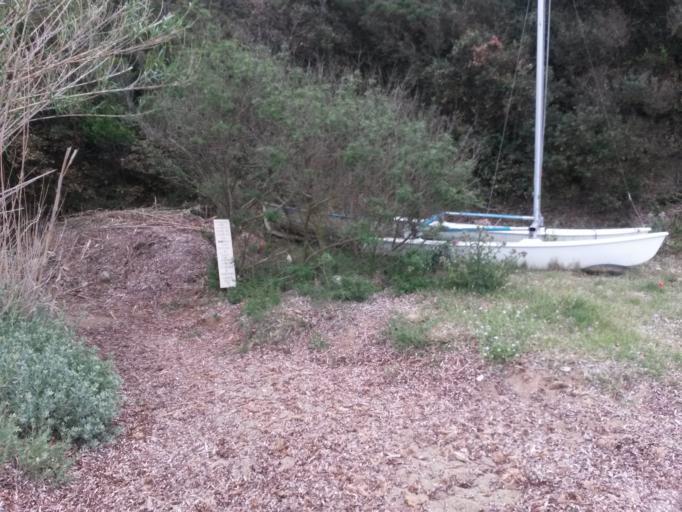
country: IT
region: Tuscany
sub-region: Provincia di Livorno
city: Capoliveri
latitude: 42.7479
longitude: 10.3615
